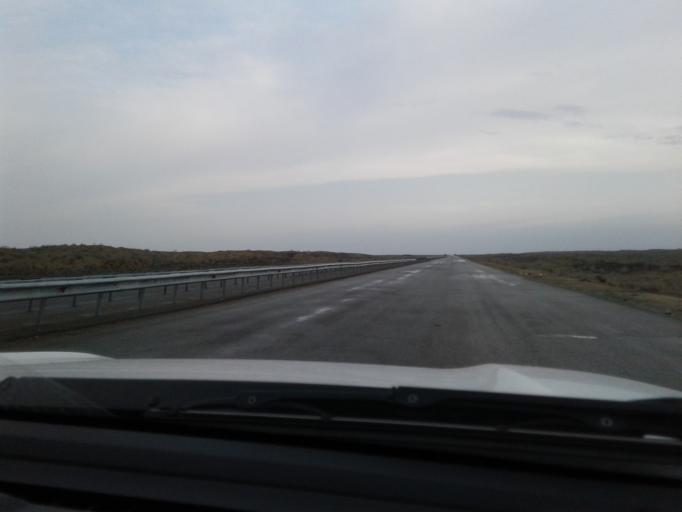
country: TM
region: Ahal
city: Abadan
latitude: 38.4897
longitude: 58.5058
